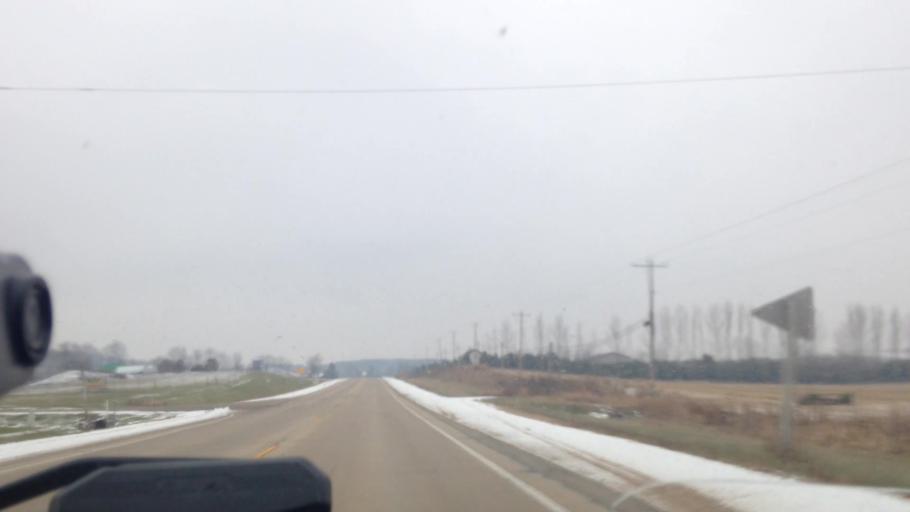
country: US
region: Wisconsin
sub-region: Dodge County
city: Mayville
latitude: 43.4728
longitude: -88.5462
